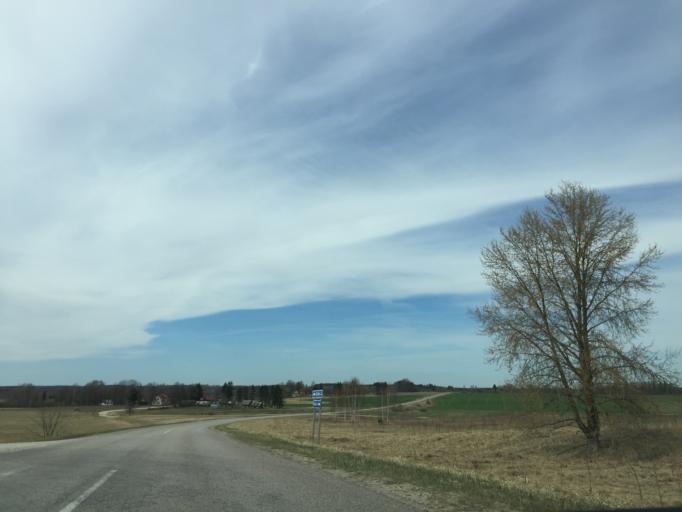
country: LV
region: Valkas Rajons
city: Valka
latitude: 57.7792
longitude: 25.9196
